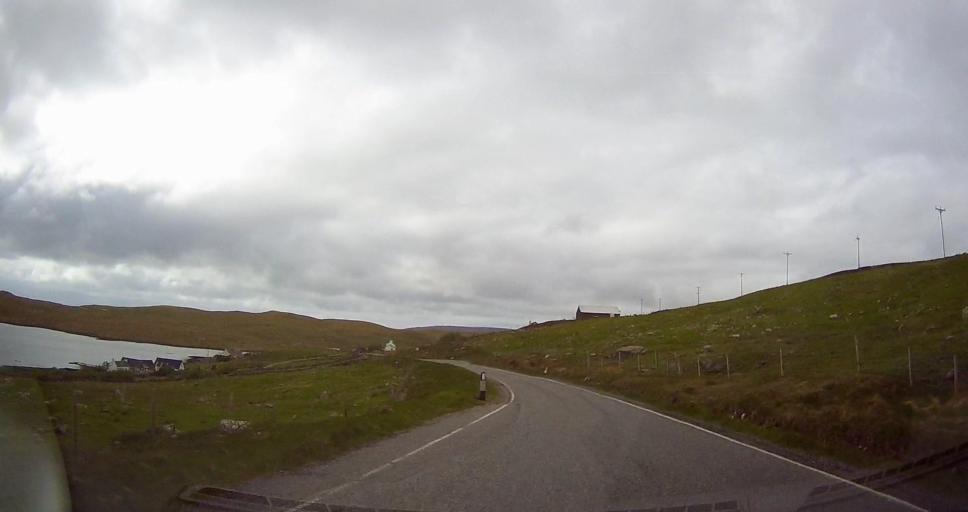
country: GB
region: Scotland
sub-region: Shetland Islands
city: Sandwick
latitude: 60.2436
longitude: -1.5152
